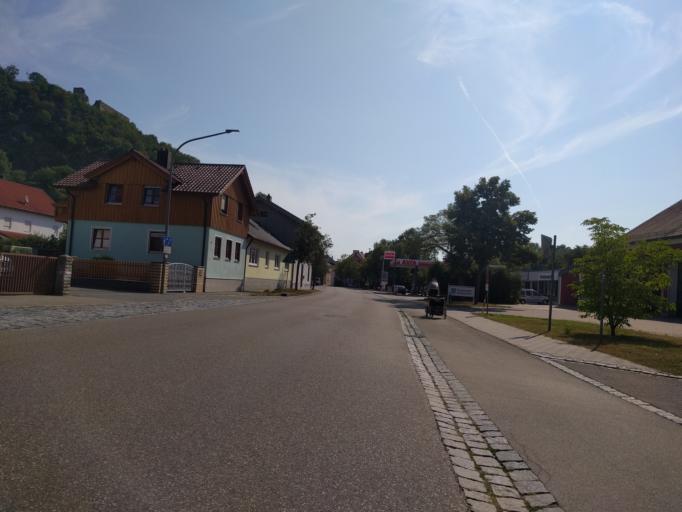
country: DE
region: Bavaria
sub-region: Upper Palatinate
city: Donaustauf
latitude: 49.0288
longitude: 12.2031
